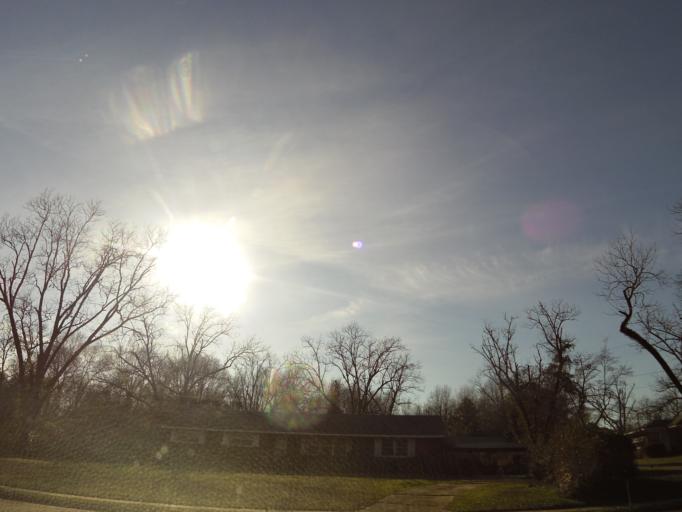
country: US
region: Georgia
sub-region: Stewart County
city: Richland
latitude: 32.0938
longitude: -84.6689
